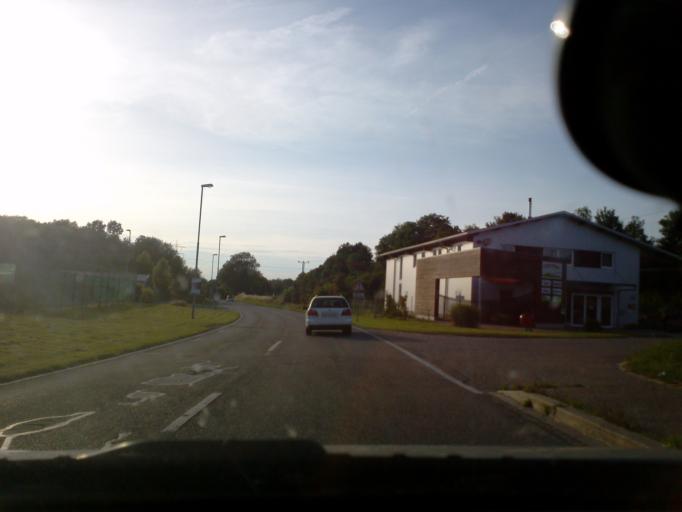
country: DE
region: Baden-Wuerttemberg
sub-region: Karlsruhe Region
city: Woessingen
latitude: 49.0181
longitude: 8.5976
